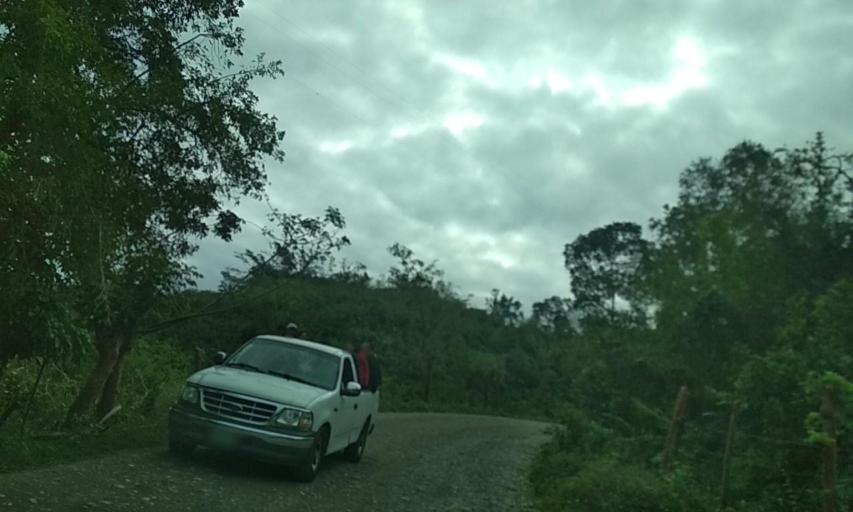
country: MX
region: Veracruz
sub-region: Papantla
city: Residencial Tajin
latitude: 20.6156
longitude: -97.3608
